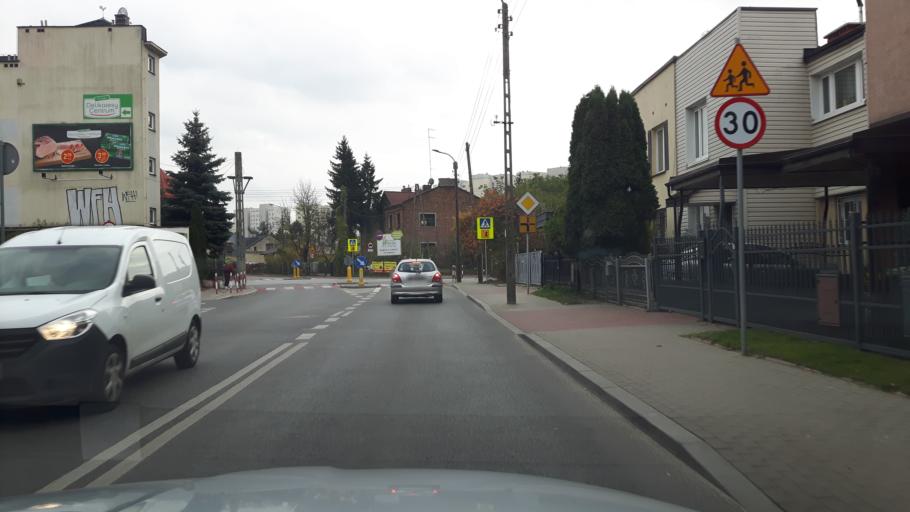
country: PL
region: Masovian Voivodeship
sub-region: Warszawa
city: Targowek
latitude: 52.2801
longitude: 21.0545
